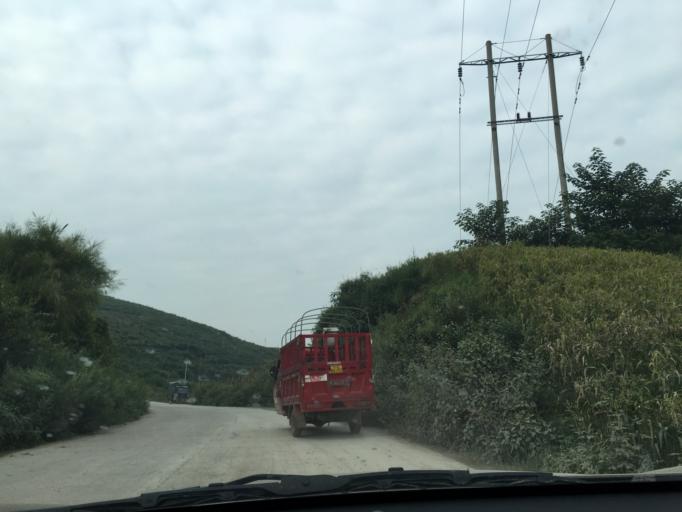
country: CN
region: Guangxi Zhuangzu Zizhiqu
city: Xinzhou
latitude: 25.4414
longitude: 105.4805
